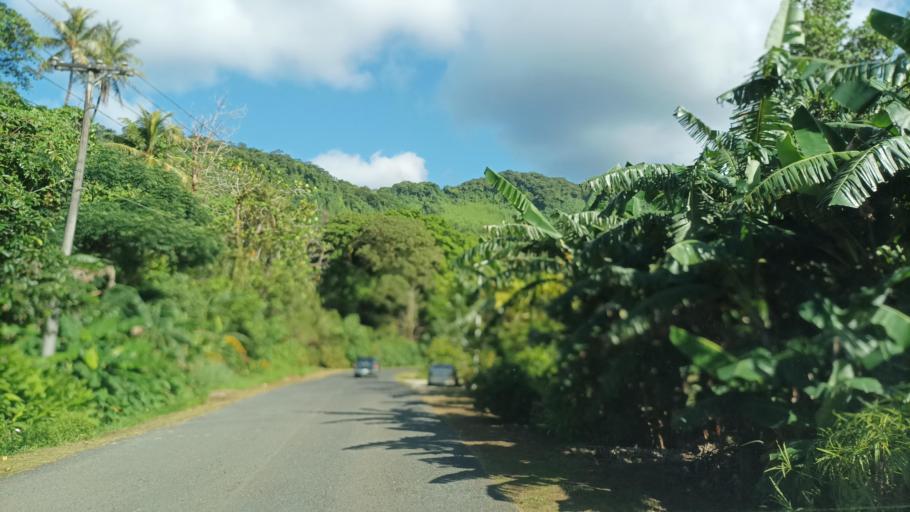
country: FM
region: Pohnpei
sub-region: Kolonia Municipality
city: Kolonia
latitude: 6.9595
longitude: 158.2487
